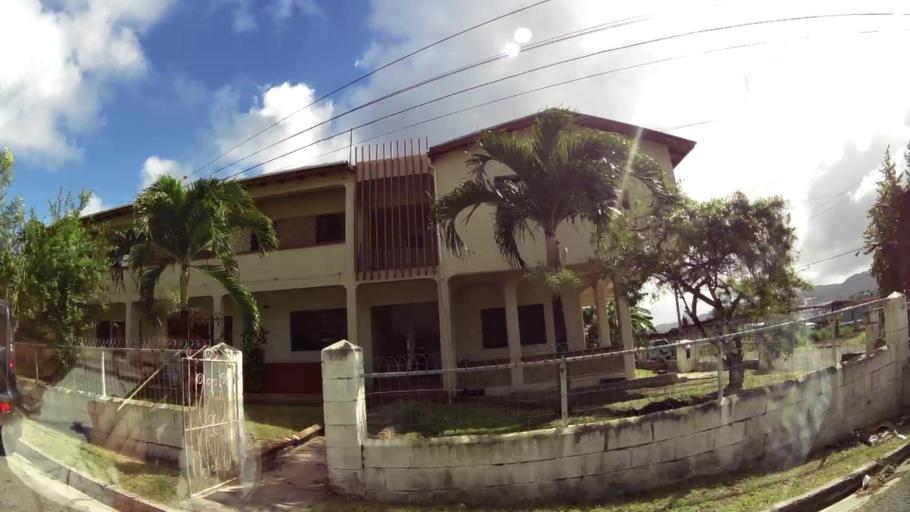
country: AG
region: Saint John
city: Saint John's
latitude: 17.1106
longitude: -61.8349
